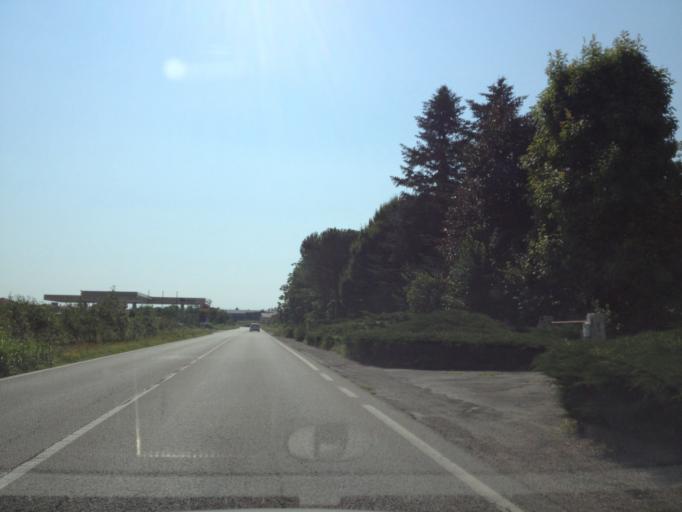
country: IT
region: Veneto
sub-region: Provincia di Vicenza
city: Cogollo del Cengio
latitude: 45.7895
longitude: 11.4104
